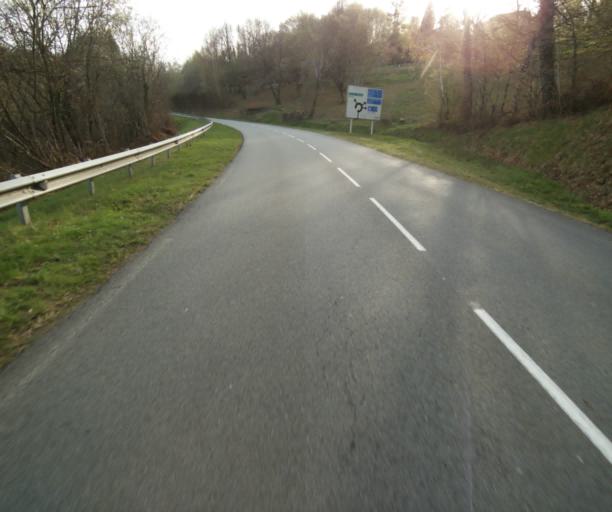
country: FR
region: Limousin
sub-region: Departement de la Correze
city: Naves
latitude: 45.3309
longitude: 1.7711
